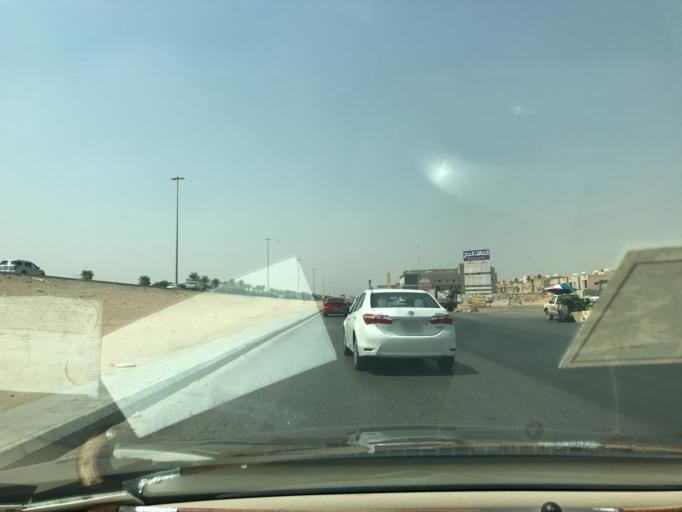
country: SA
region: Ar Riyad
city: Riyadh
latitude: 24.8235
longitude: 46.7946
